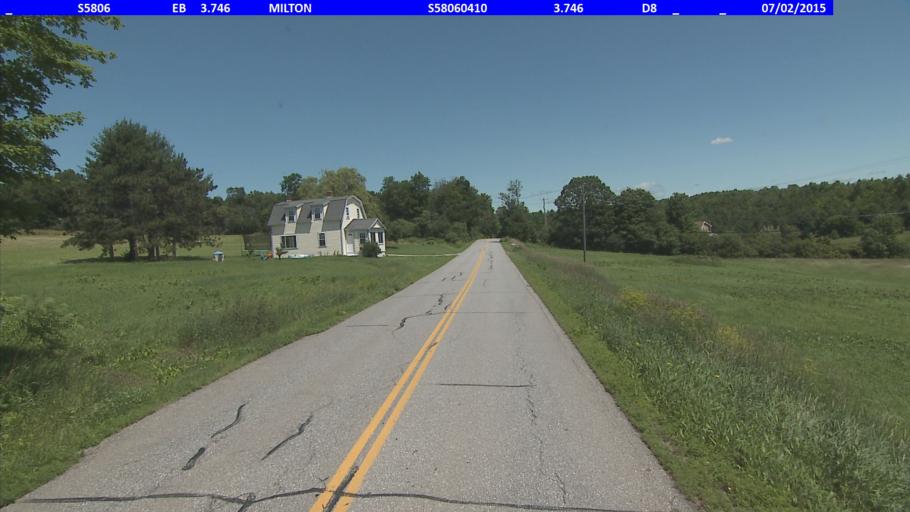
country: US
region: Vermont
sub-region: Chittenden County
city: Milton
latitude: 44.6755
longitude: -73.1757
